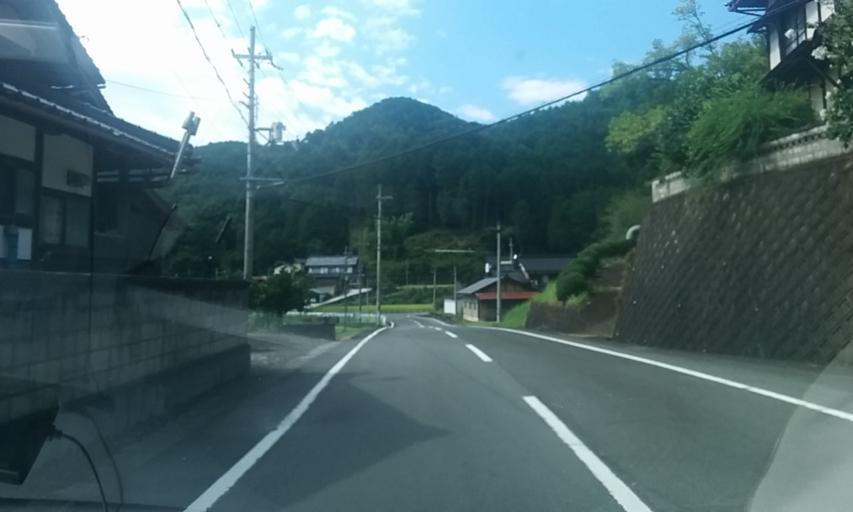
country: JP
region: Kyoto
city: Fukuchiyama
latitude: 35.3725
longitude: 135.1576
